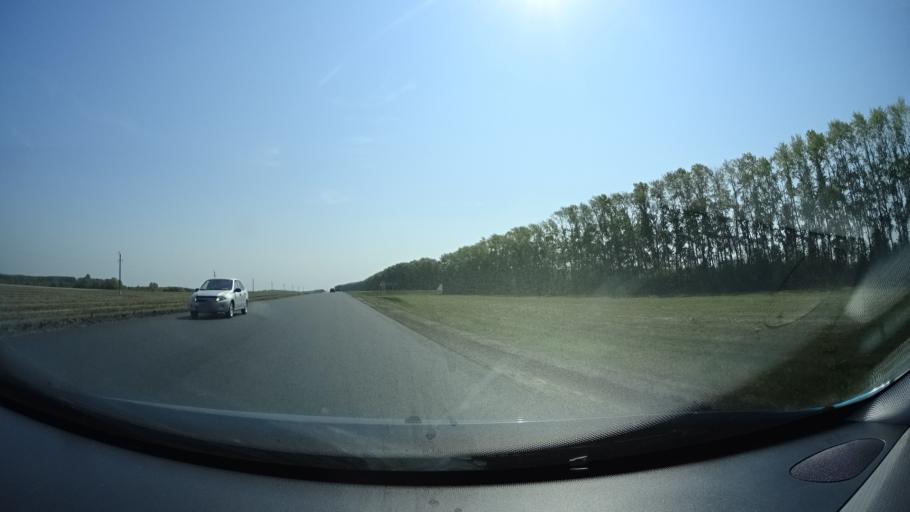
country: RU
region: Bashkortostan
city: Karmaskaly
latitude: 54.4099
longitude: 56.0688
